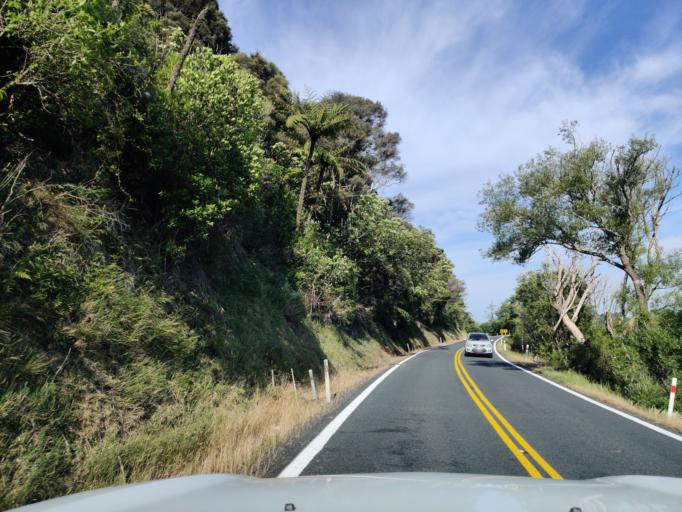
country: NZ
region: Waikato
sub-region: Waikato District
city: Ngaruawahia
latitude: -37.6317
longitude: 175.1580
